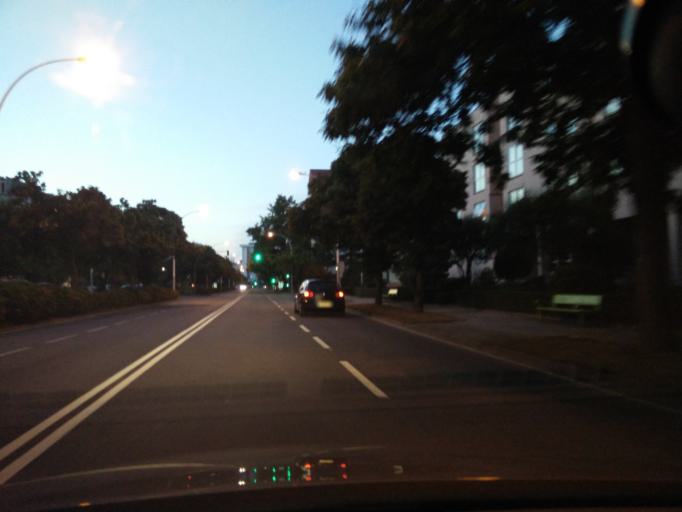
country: ES
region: Galicia
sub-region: Provincia da Coruna
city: A Coruna
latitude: 43.3450
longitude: -8.4066
